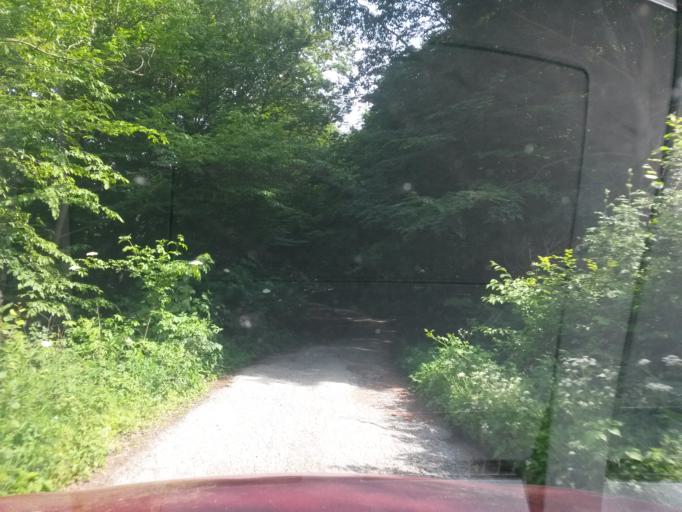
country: SK
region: Kosicky
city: Kosice
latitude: 48.7358
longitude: 21.1192
